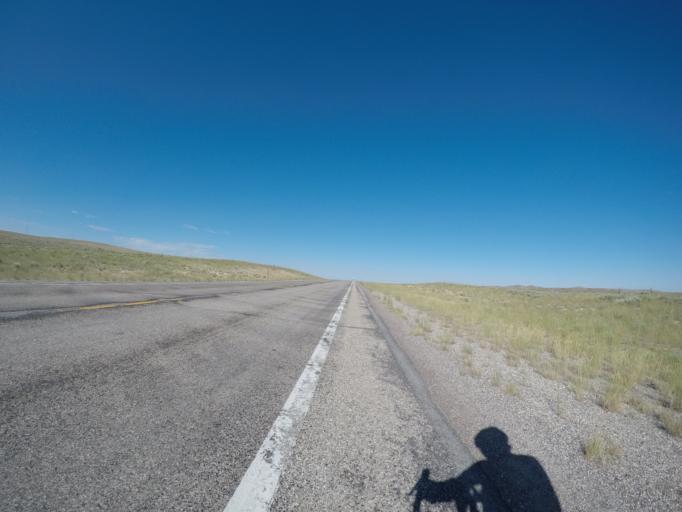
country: US
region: Wyoming
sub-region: Carbon County
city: Saratoga
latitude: 41.8884
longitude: -106.4675
